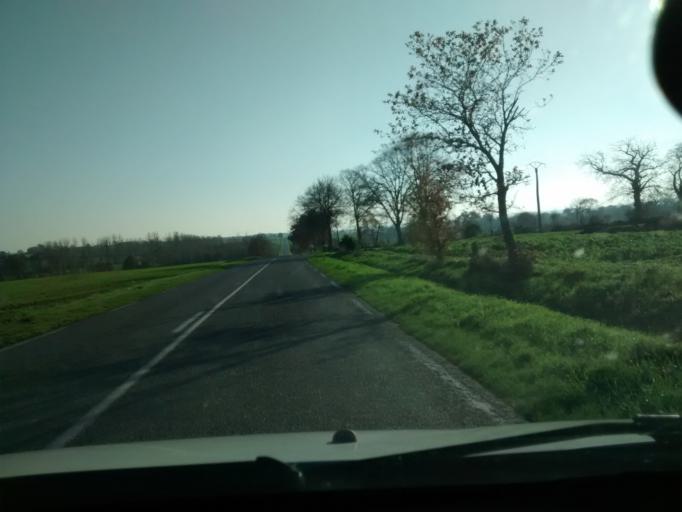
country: FR
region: Lower Normandy
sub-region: Departement de la Manche
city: Pontorson
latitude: 48.5188
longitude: -1.4813
